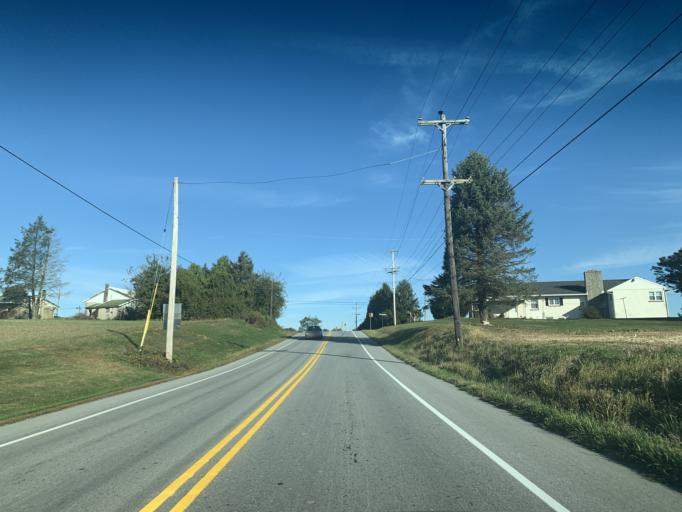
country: US
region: Pennsylvania
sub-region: Chester County
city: Parkesburg
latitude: 39.9167
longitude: -75.9125
